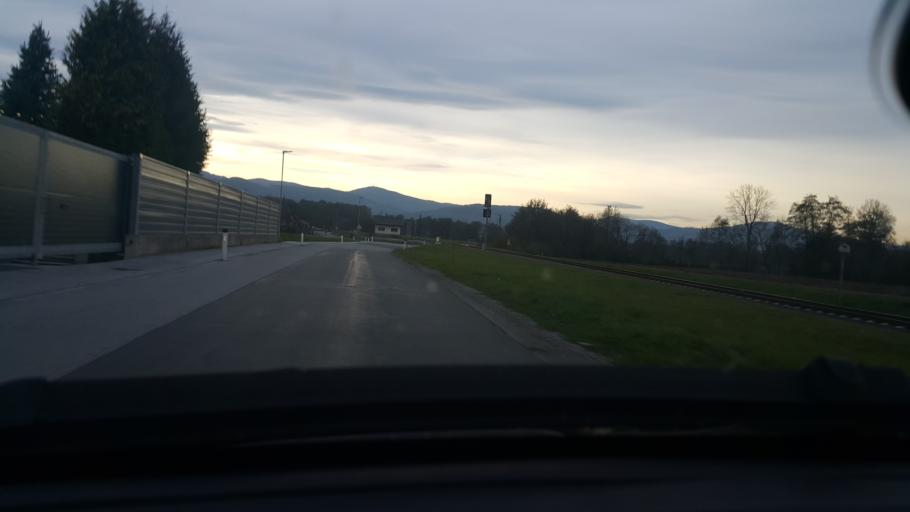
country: AT
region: Styria
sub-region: Politischer Bezirk Deutschlandsberg
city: Sankt Martin im Sulmtal
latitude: 46.7495
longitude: 15.2808
